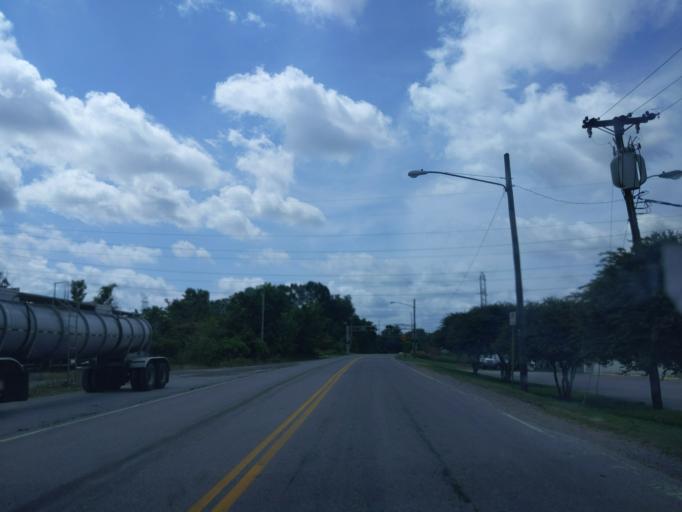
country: US
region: Tennessee
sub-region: Davidson County
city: Nashville
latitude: 36.1574
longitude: -86.7437
